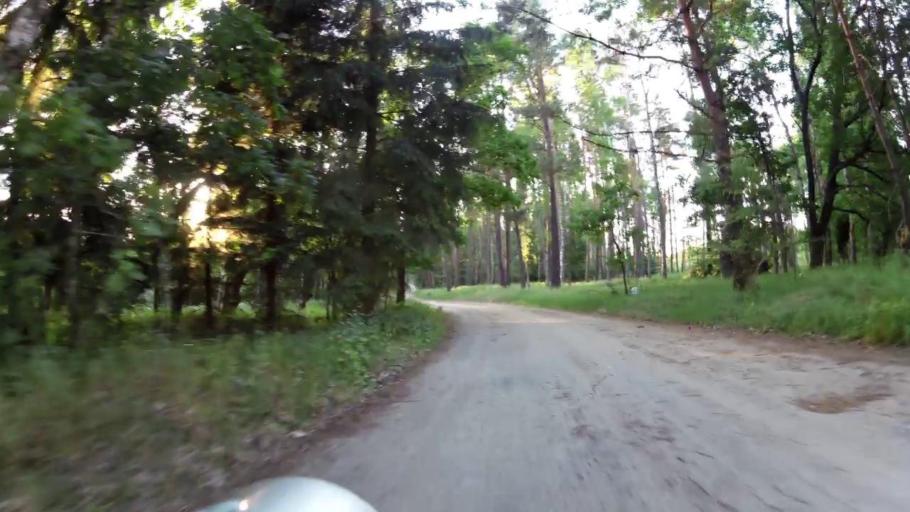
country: PL
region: West Pomeranian Voivodeship
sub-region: Powiat szczecinecki
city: Szczecinek
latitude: 53.8167
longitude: 16.6972
